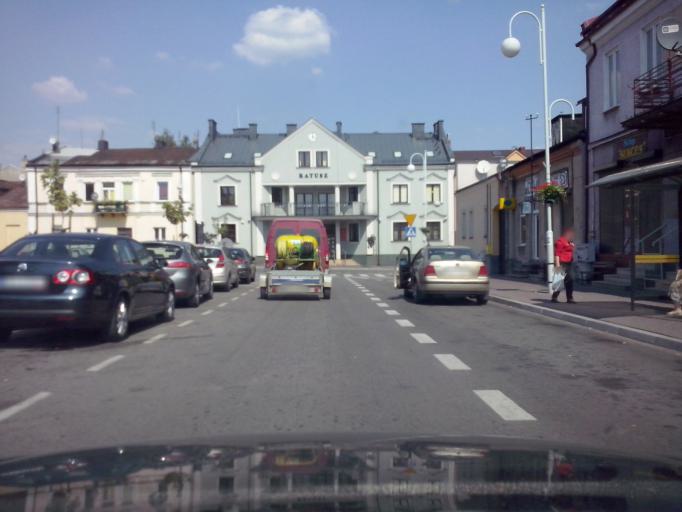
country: PL
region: Swietokrzyskie
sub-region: Powiat kielecki
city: Chmielnik
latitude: 50.6144
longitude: 20.7521
